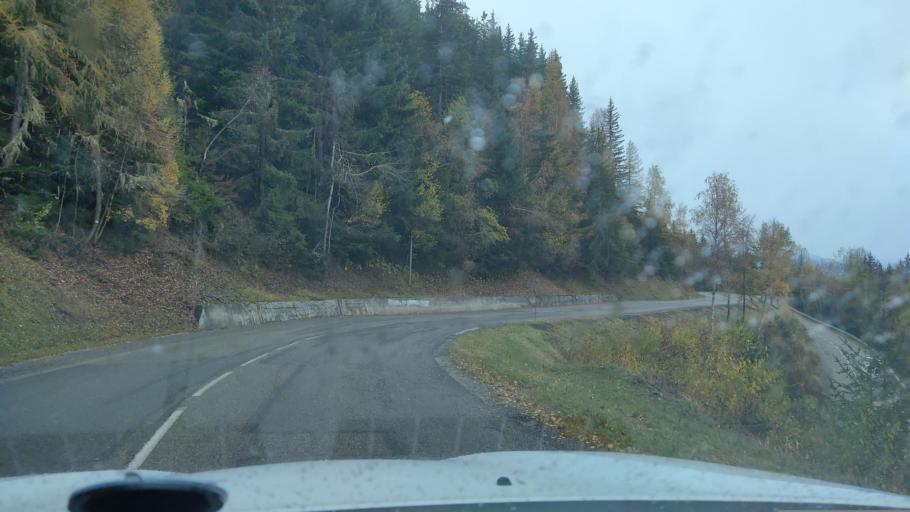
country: FR
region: Rhone-Alpes
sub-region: Departement de la Savoie
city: Bourg-Saint-Maurice
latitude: 45.5814
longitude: 6.7757
